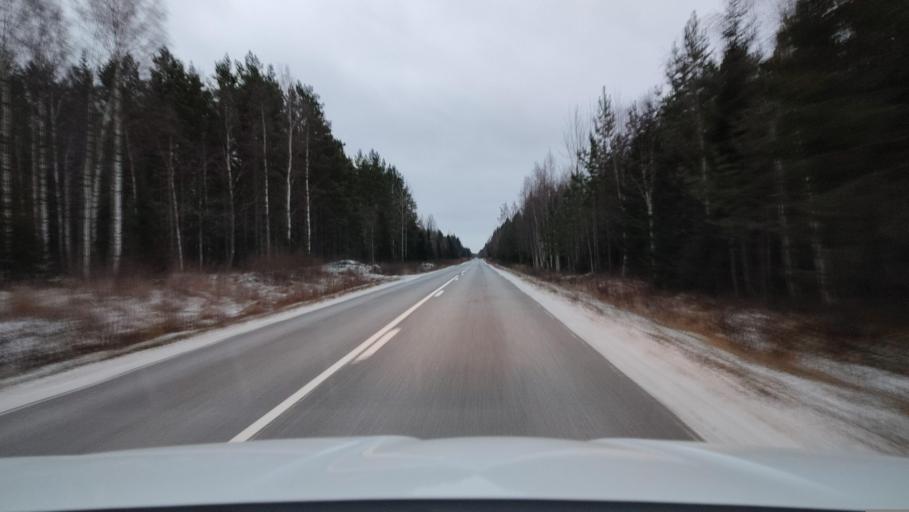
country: FI
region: Ostrobothnia
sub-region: Vaasa
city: Replot
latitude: 63.2633
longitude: 21.3593
